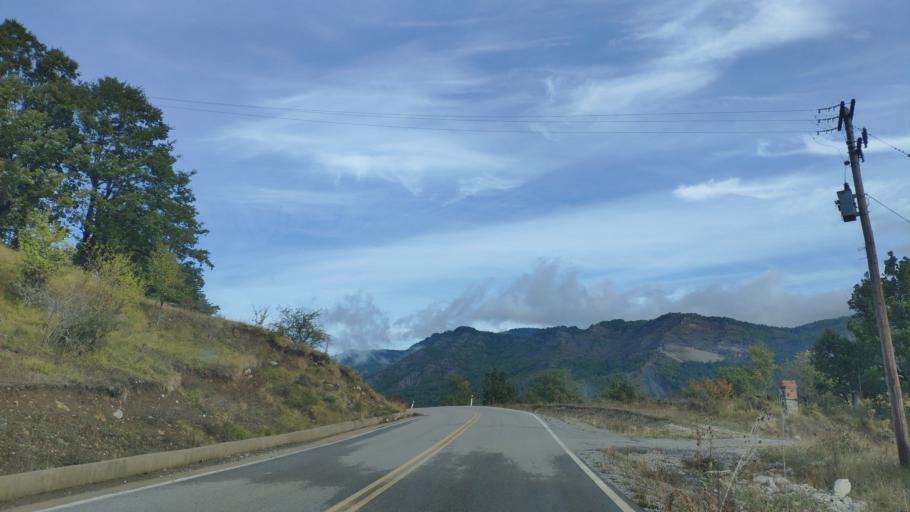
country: GR
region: West Macedonia
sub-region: Nomos Kastorias
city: Nestorio
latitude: 40.2784
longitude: 20.9742
